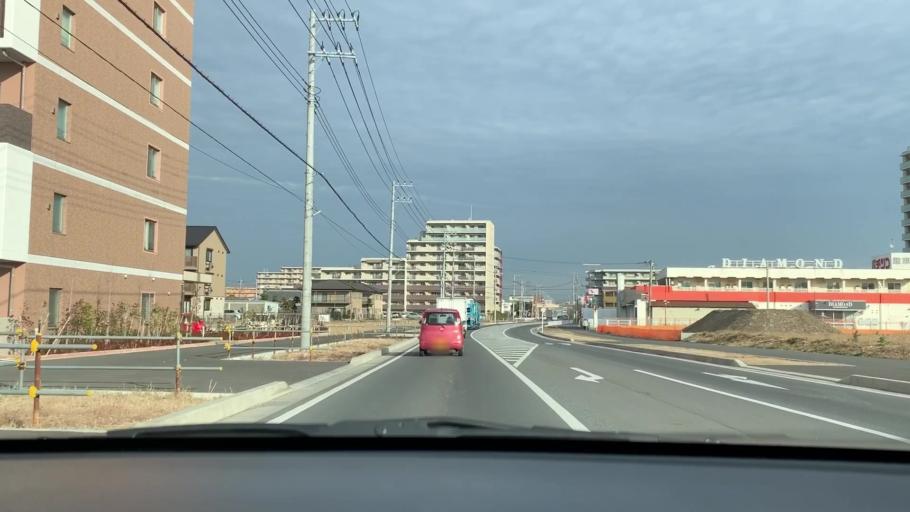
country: JP
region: Chiba
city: Nagareyama
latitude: 35.8337
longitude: 139.8959
